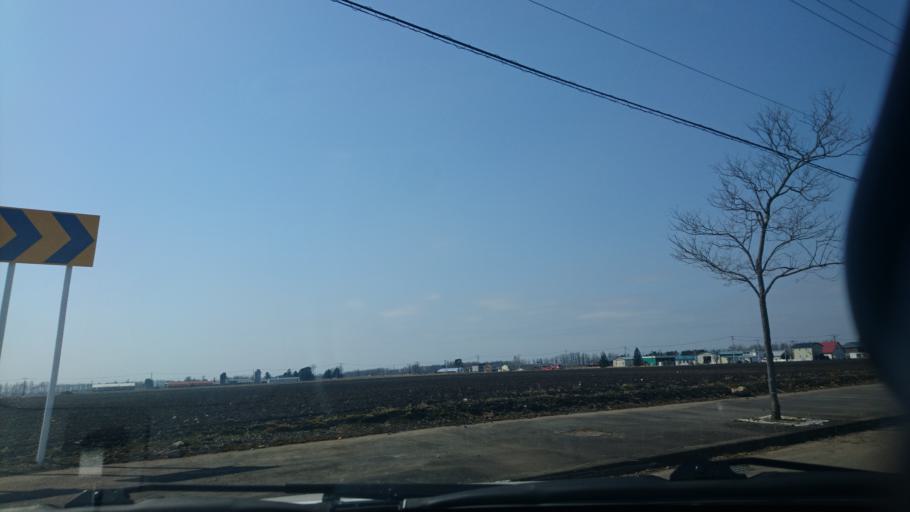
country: JP
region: Hokkaido
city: Otofuke
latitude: 43.0934
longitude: 143.2321
